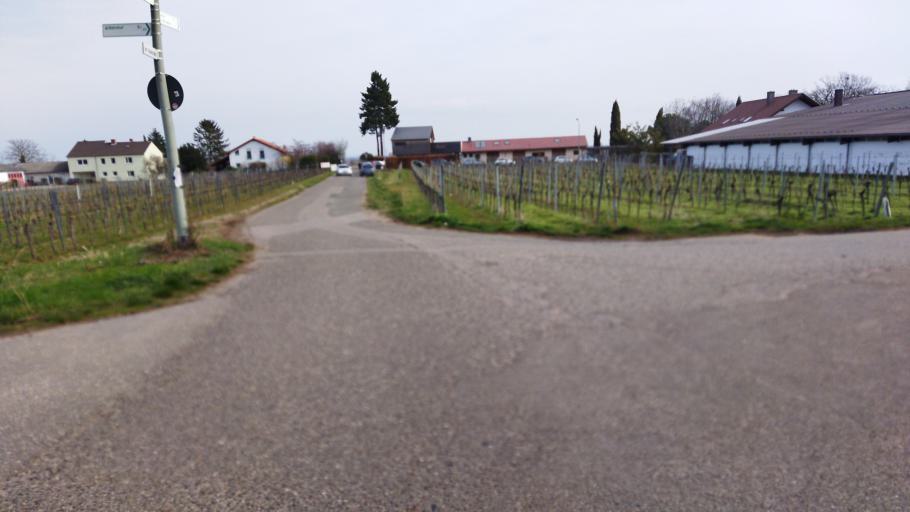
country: DE
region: Rheinland-Pfalz
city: Ruppertsberg
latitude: 49.3736
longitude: 8.1707
